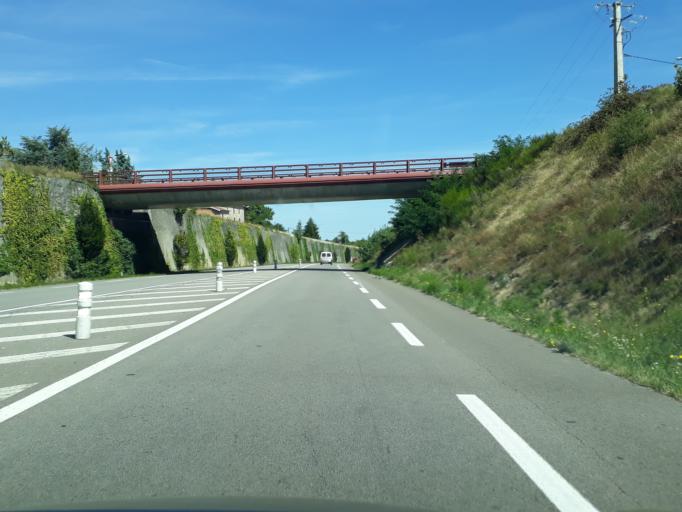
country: FR
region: Rhone-Alpes
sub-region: Departement de l'Ardeche
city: Peaugres
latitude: 45.2778
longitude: 4.7223
